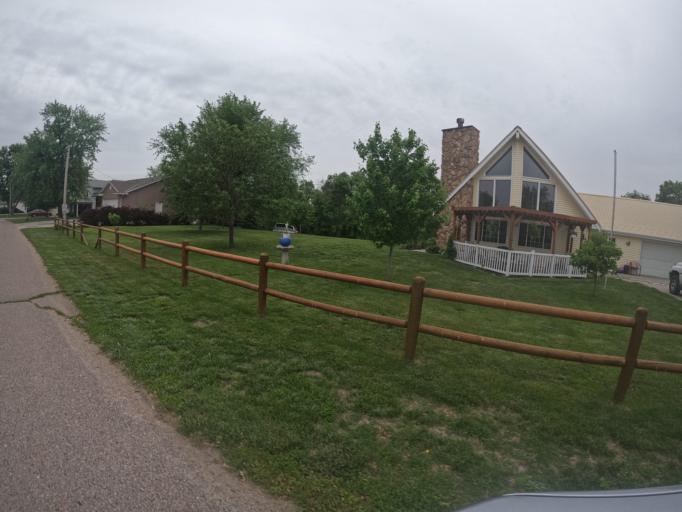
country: US
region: Nebraska
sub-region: Sarpy County
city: Offutt Air Force Base
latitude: 41.0529
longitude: -95.9542
